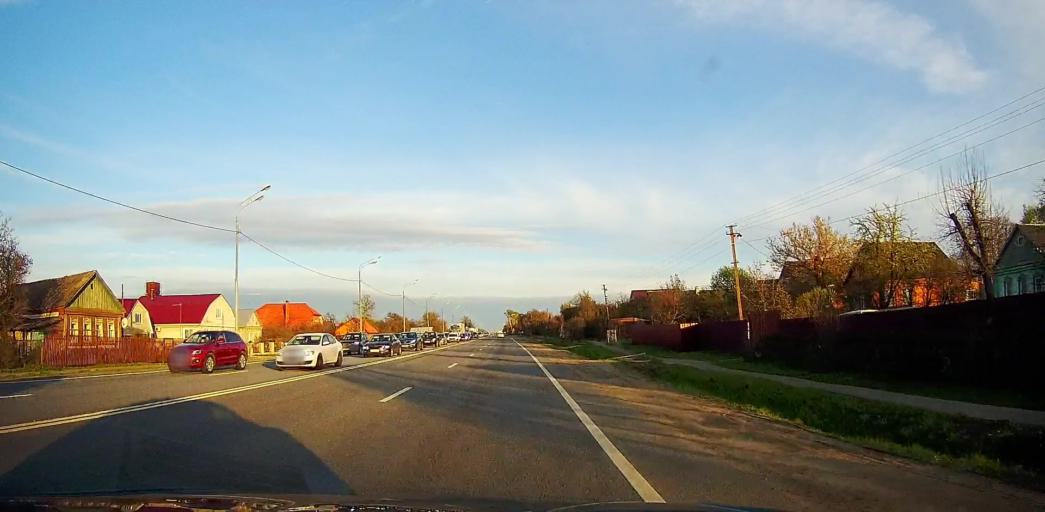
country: RU
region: Moskovskaya
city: Troitskoye
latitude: 55.2453
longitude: 38.5317
